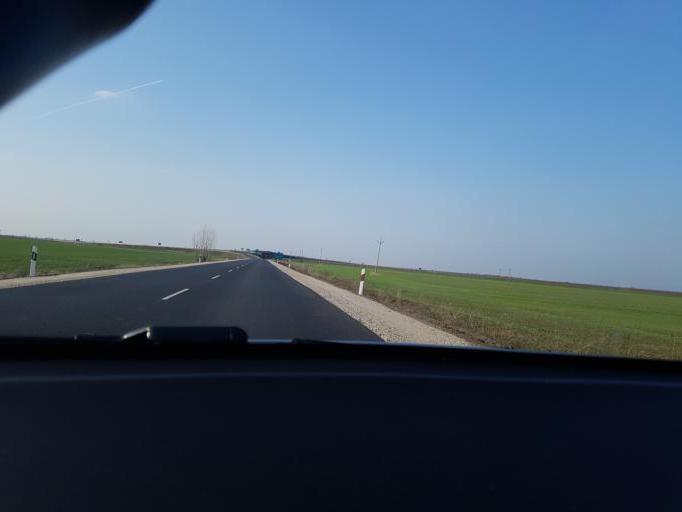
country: HU
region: Csongrad
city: Csanadpalota
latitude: 46.2104
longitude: 20.7177
